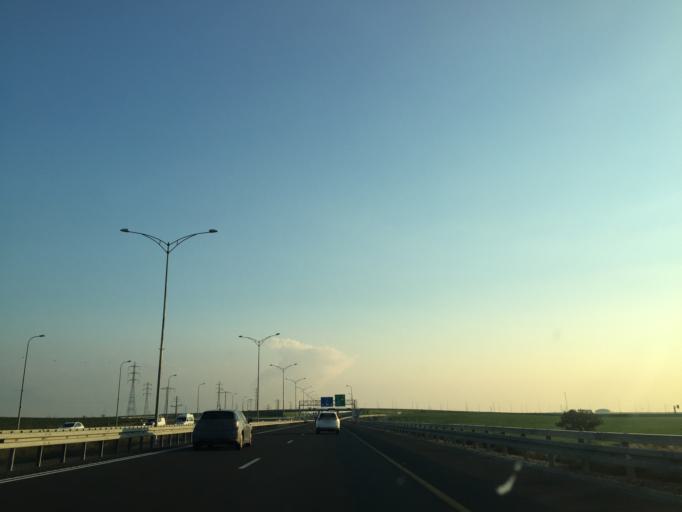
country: IL
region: Southern District
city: Lehavim
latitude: 31.4489
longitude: 34.7707
